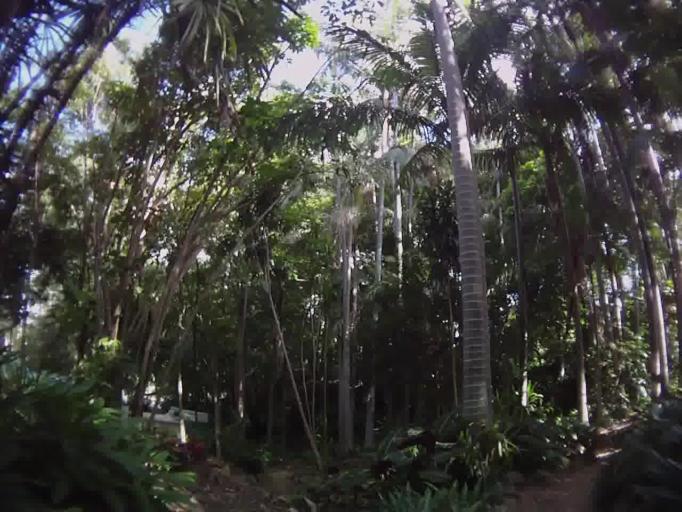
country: AU
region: Queensland
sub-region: Brisbane
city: Brisbane
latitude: -27.4778
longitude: 153.0309
